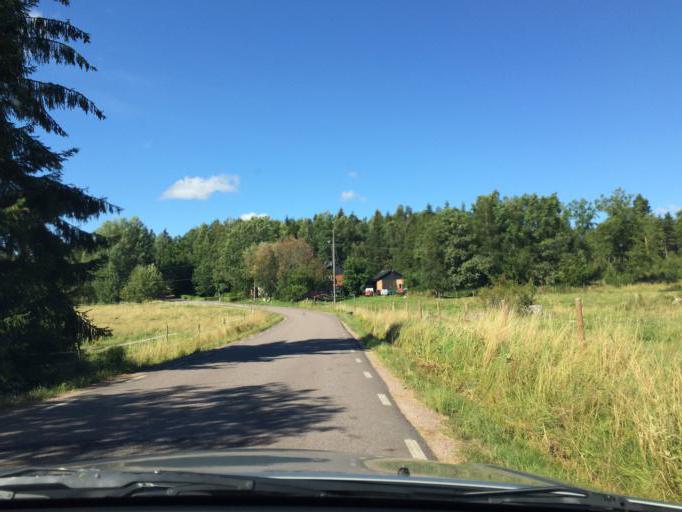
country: SE
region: Soedermanland
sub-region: Eskilstuna Kommun
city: Kvicksund
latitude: 59.5078
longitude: 16.3977
